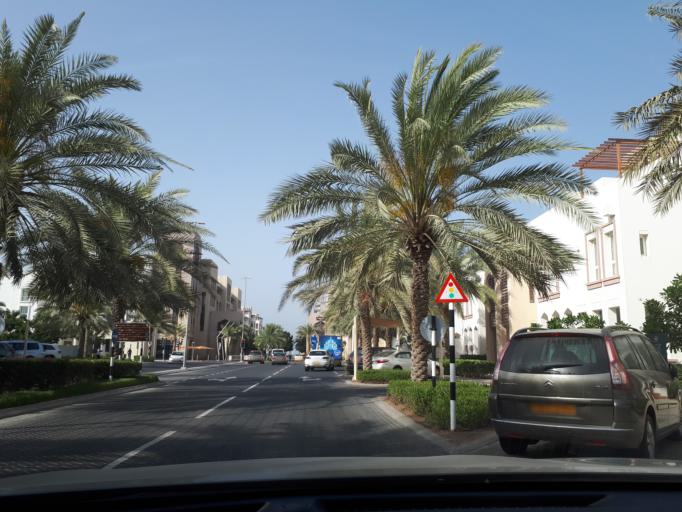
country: OM
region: Muhafazat Masqat
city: As Sib al Jadidah
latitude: 23.6276
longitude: 58.2656
